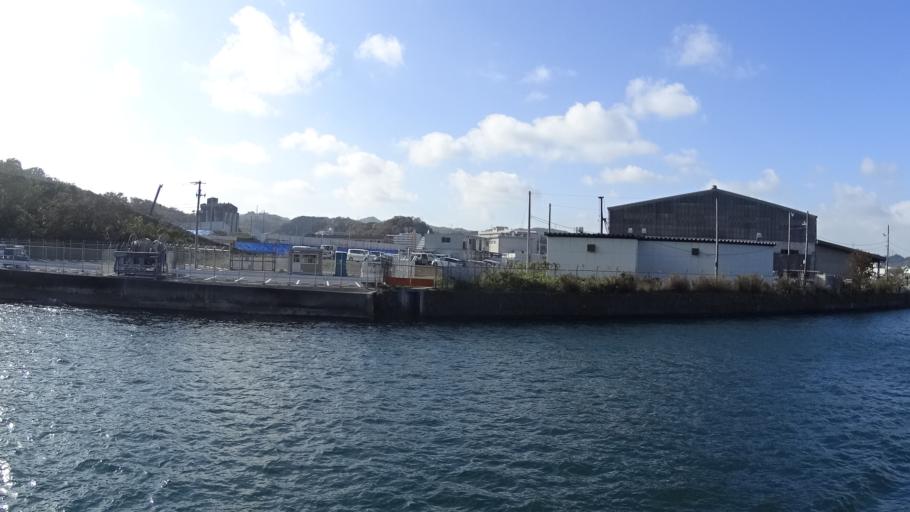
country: JP
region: Kanagawa
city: Yokosuka
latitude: 35.2980
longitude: 139.6448
